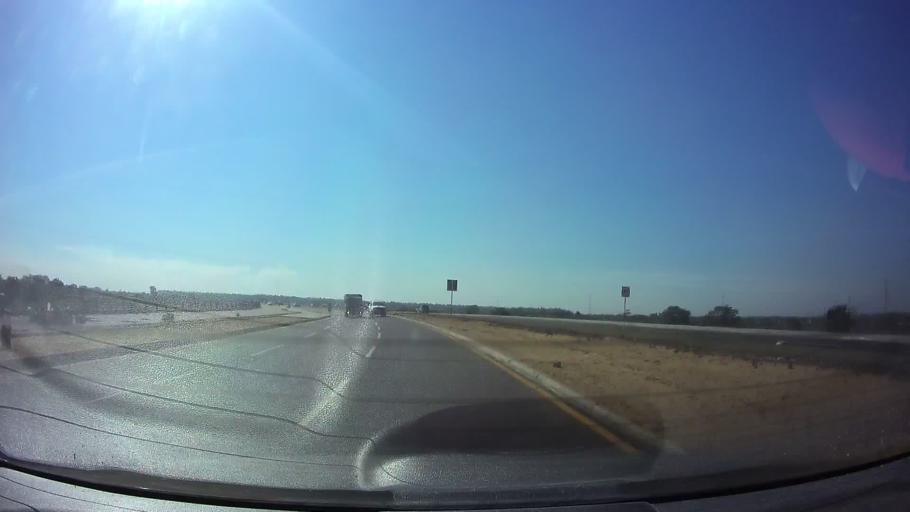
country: PY
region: Asuncion
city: Asuncion
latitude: -25.2619
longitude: -57.6072
